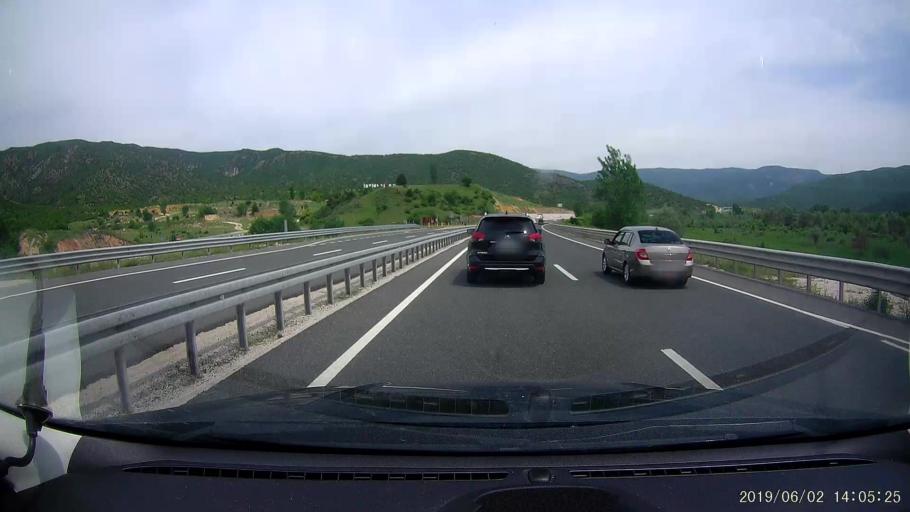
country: TR
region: Cankiri
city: Ilgaz
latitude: 40.9014
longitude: 33.6684
